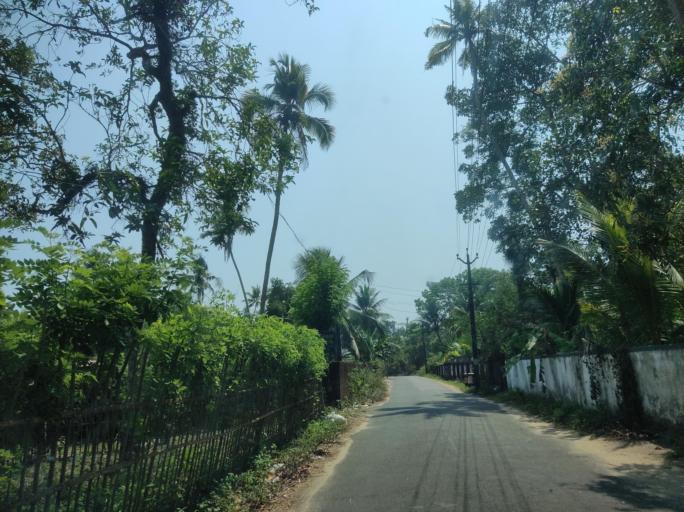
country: IN
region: Kerala
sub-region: Alappuzha
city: Vayalar
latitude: 9.6979
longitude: 76.3035
